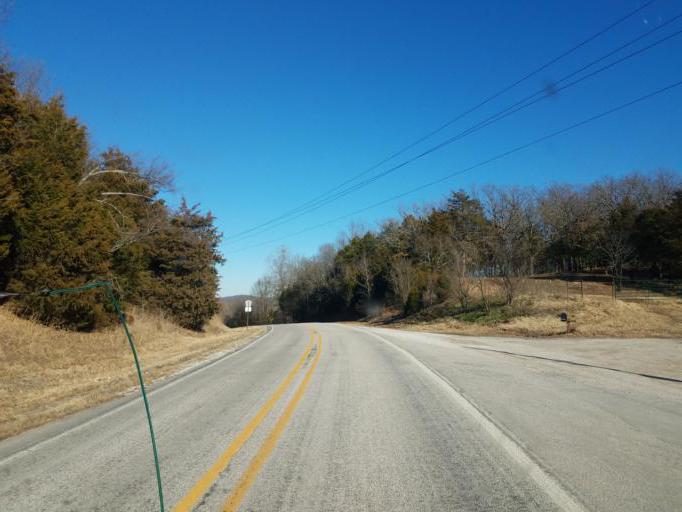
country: US
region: Arkansas
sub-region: Washington County
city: Elkins
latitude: 36.0250
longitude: -93.9870
